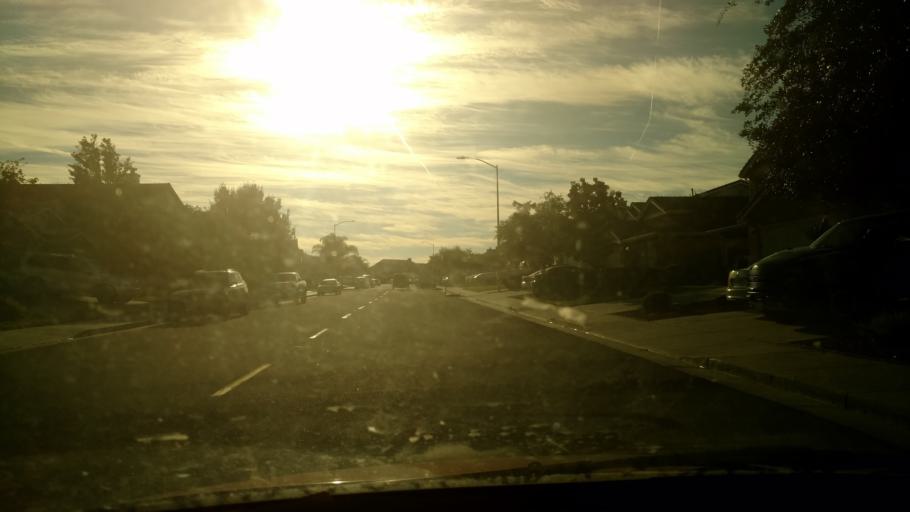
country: US
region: California
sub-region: San Benito County
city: Ridgemark
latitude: 36.8223
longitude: -121.3745
